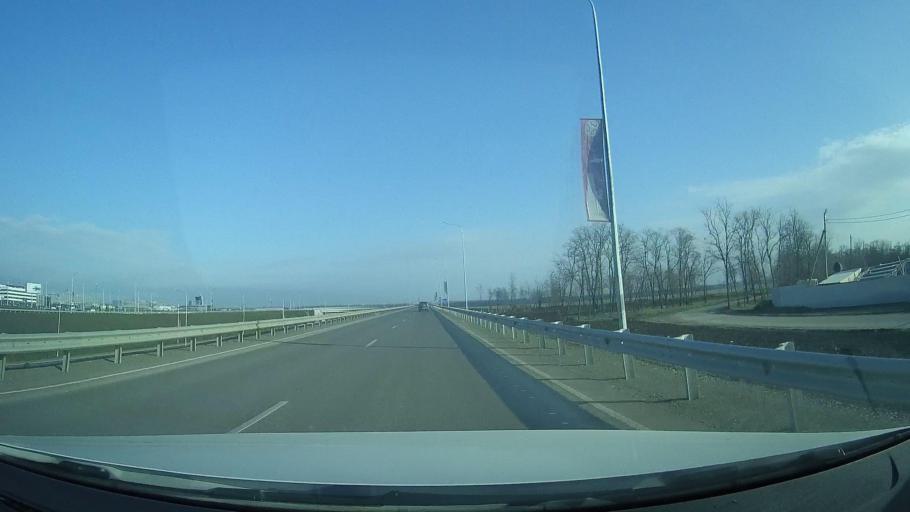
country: RU
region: Rostov
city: Grushevskaya
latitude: 47.4849
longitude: 39.9340
